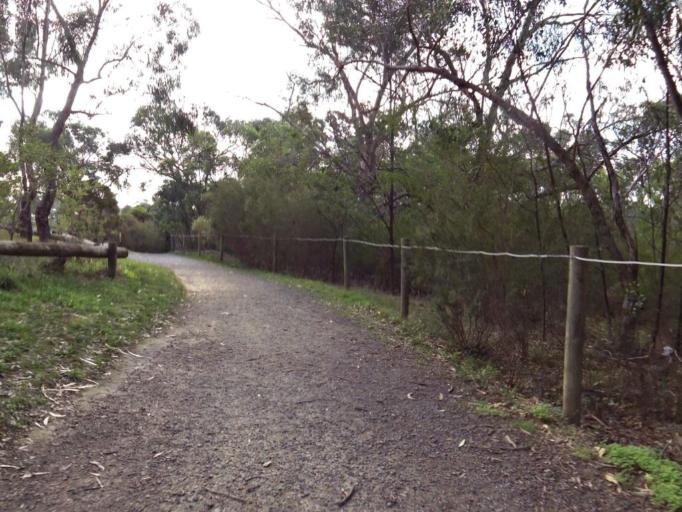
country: AU
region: Victoria
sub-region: Manningham
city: Park Orchards
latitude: -37.7763
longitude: 145.2200
